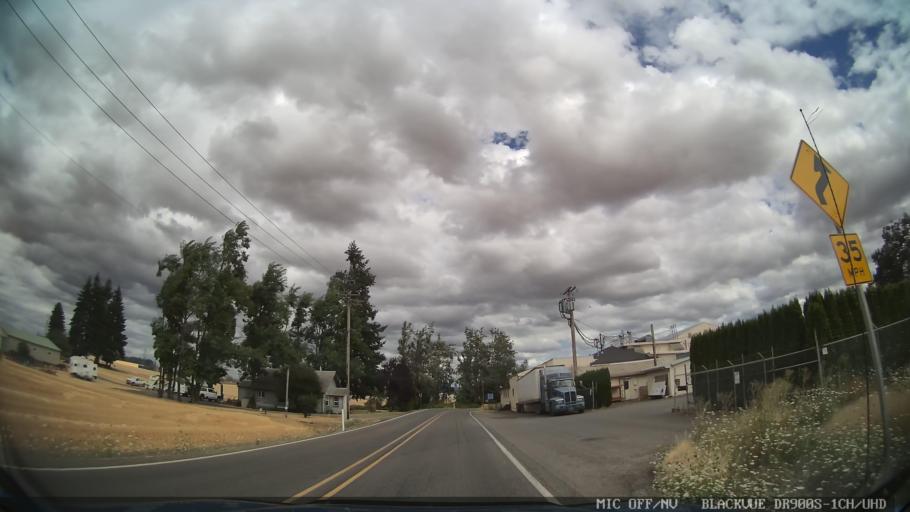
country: US
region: Oregon
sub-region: Marion County
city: Sublimity
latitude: 44.8669
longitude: -122.8036
